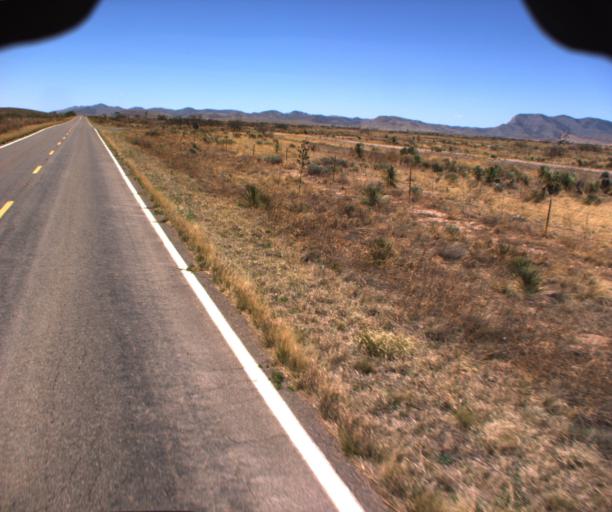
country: US
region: Arizona
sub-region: Cochise County
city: Douglas
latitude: 31.6331
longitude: -109.1939
